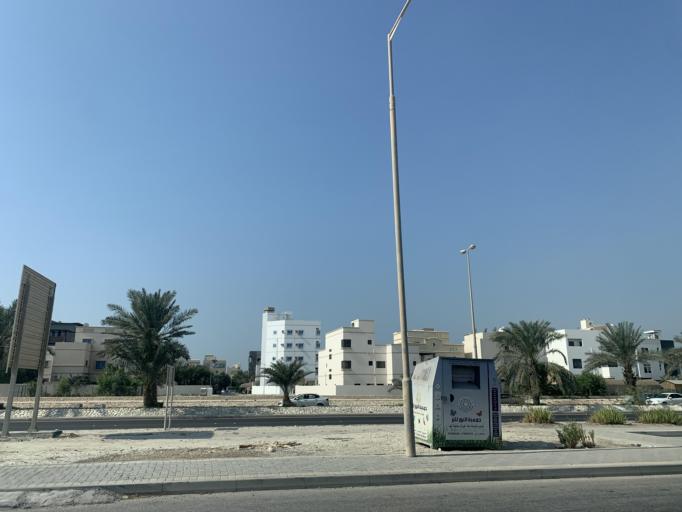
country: BH
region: Central Governorate
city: Madinat Hamad
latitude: 26.1016
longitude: 50.4993
